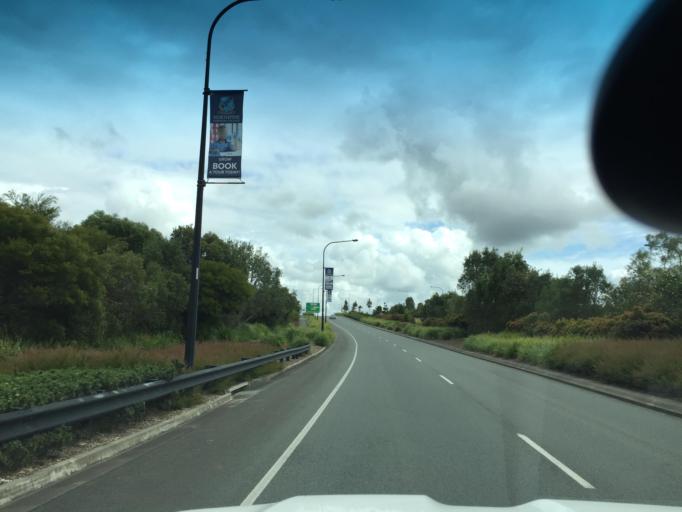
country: AU
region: Queensland
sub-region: Moreton Bay
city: Deception Bay
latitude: -27.2125
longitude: 152.9993
